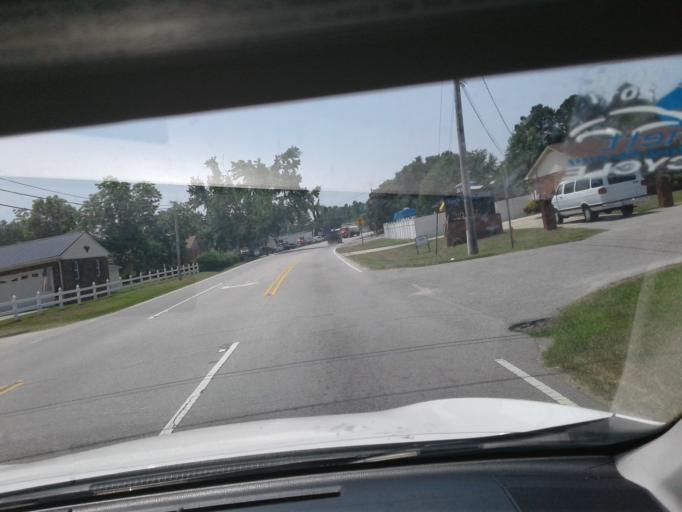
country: US
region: North Carolina
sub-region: Harnett County
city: Erwin
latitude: 35.3241
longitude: -78.6775
